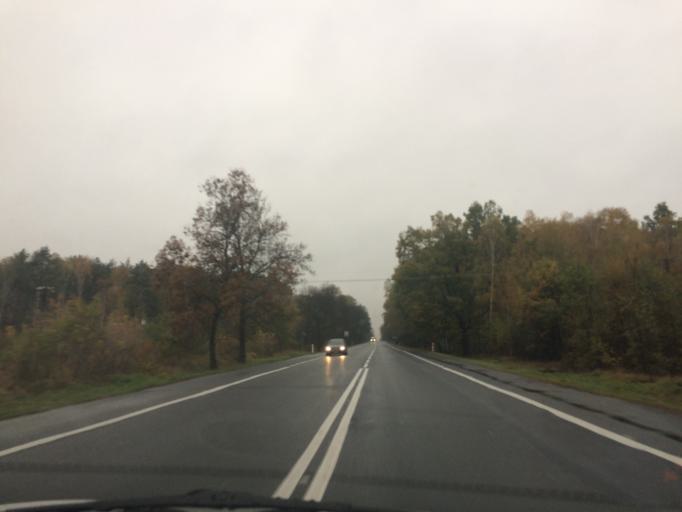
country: PL
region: Masovian Voivodeship
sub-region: Powiat otwocki
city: Kolbiel
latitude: 52.0793
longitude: 21.4417
